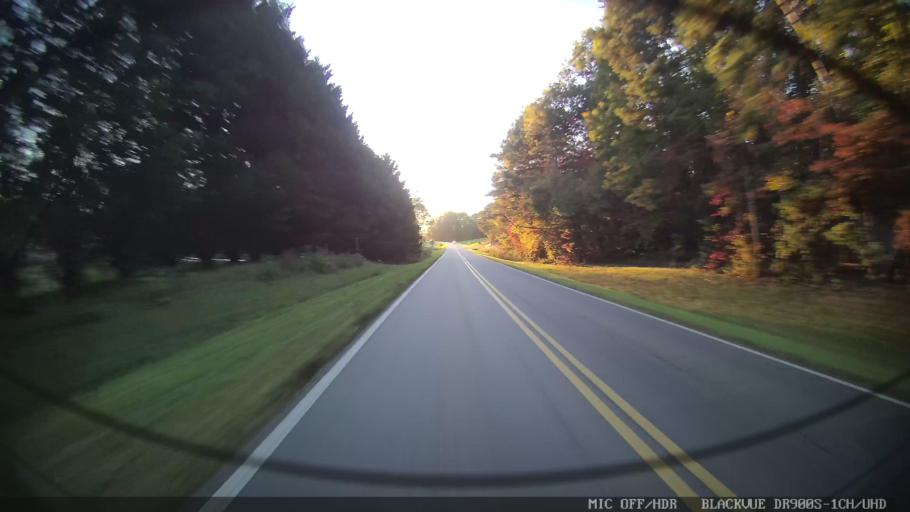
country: US
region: Georgia
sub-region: Union County
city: Blairsville
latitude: 34.8462
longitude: -83.9264
